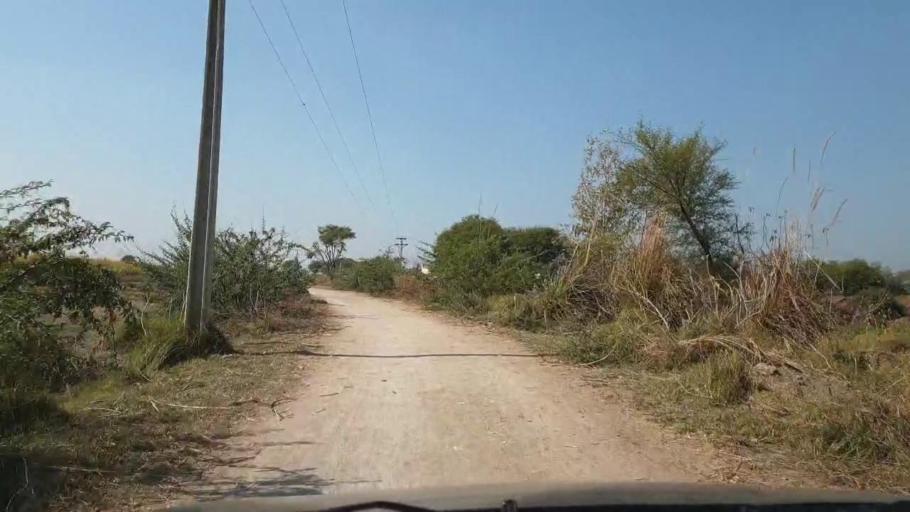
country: PK
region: Sindh
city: Jhol
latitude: 25.9119
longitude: 68.8183
